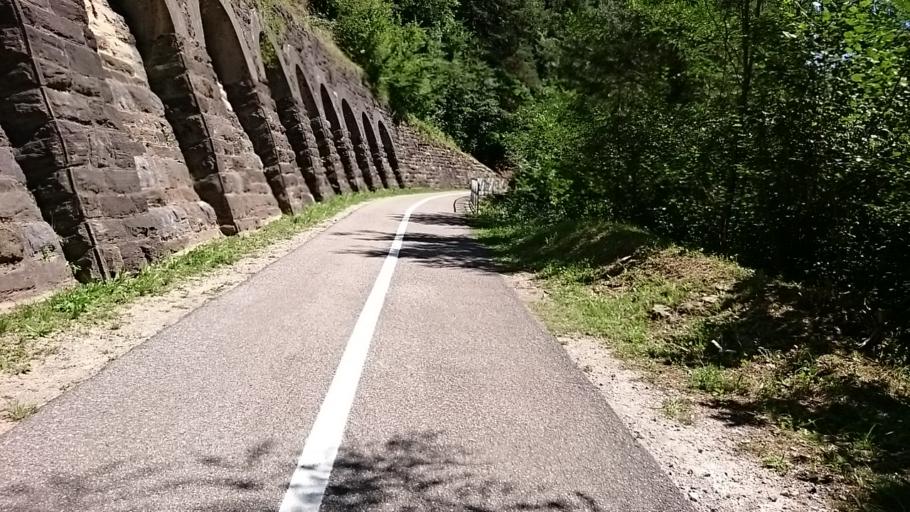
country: IT
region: Veneto
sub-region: Provincia di Belluno
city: Valle di Cadore
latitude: 46.4166
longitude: 12.3189
